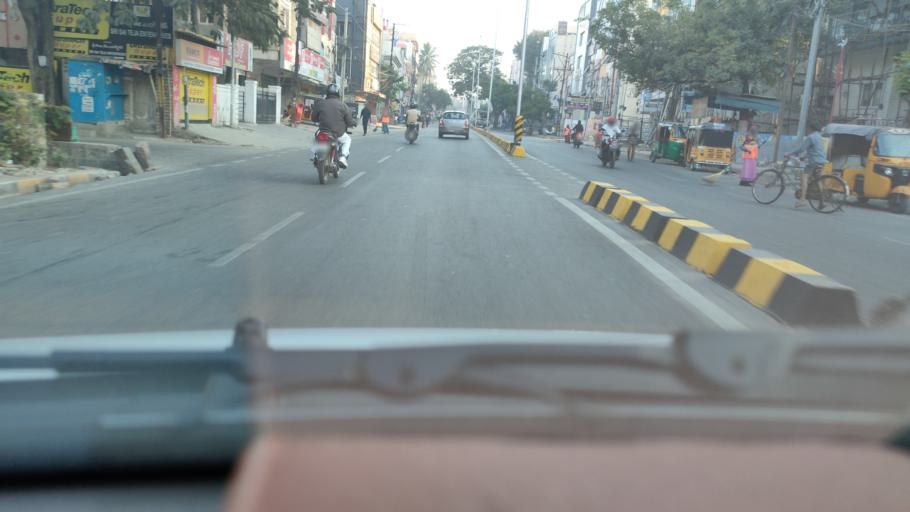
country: IN
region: Telangana
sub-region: Rangareddi
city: Gaddi Annaram
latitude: 17.3963
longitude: 78.5115
